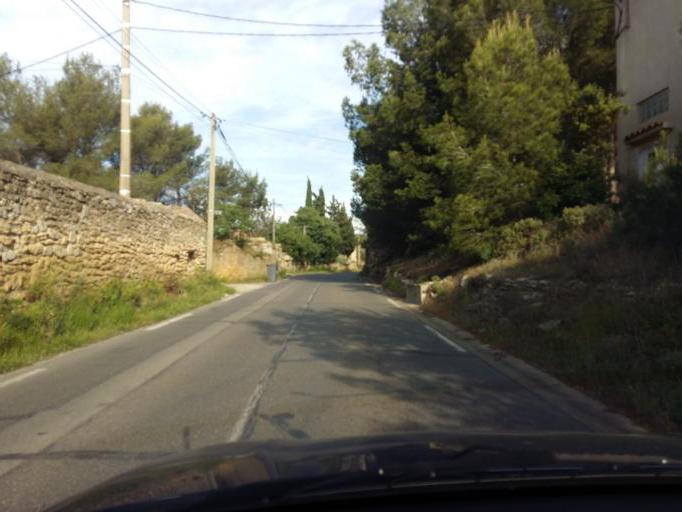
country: FR
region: Provence-Alpes-Cote d'Azur
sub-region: Departement des Bouches-du-Rhone
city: Salon-de-Provence
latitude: 43.6369
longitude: 5.1222
